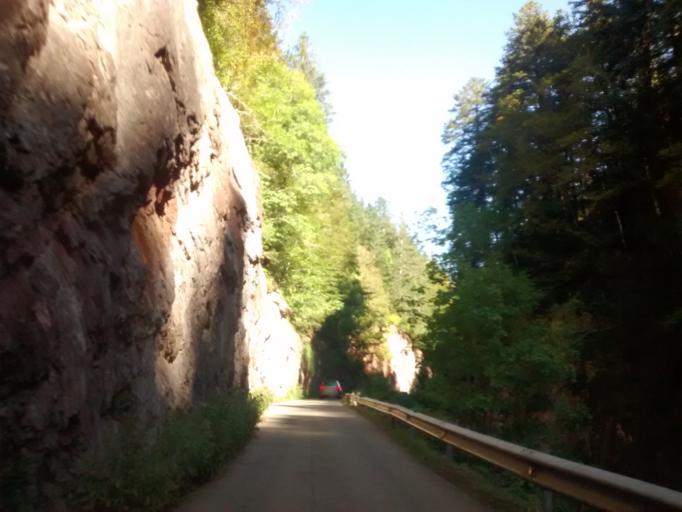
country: ES
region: Aragon
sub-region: Provincia de Huesca
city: Aragues del Puerto
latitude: 42.8273
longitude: -0.7115
